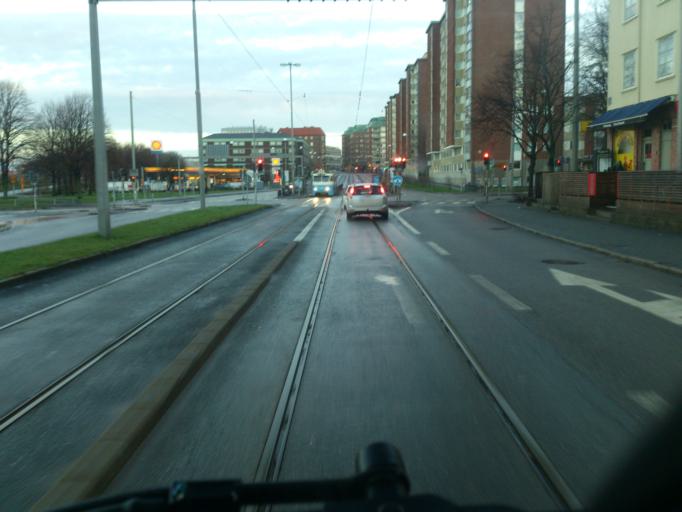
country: SE
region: Vaestra Goetaland
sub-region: Goteborg
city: Majorna
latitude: 57.6909
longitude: 11.9141
